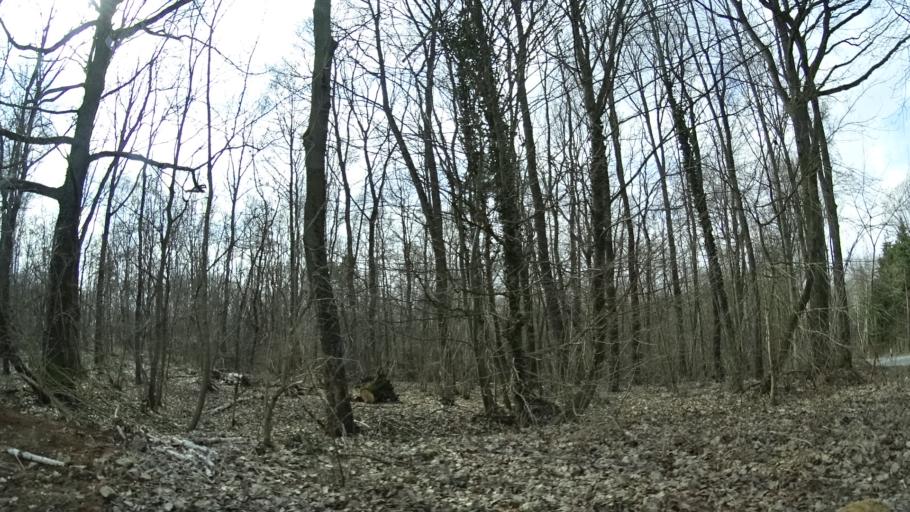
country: DE
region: Saxony-Anhalt
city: Schonburg
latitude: 51.1568
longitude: 11.8825
